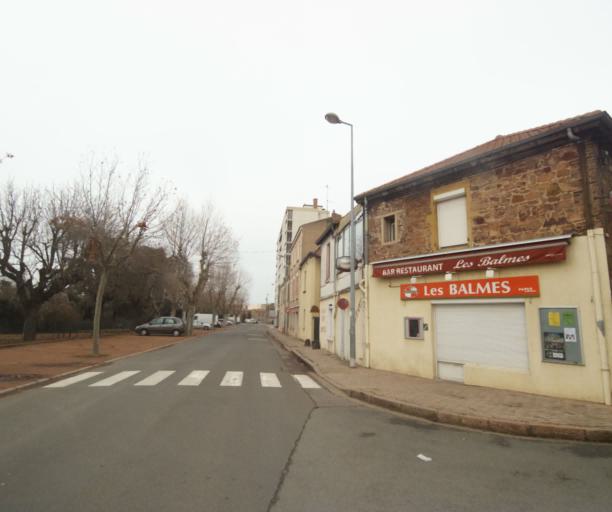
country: FR
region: Rhone-Alpes
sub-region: Departement de la Loire
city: Le Coteau
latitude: 46.0265
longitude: 4.0824
